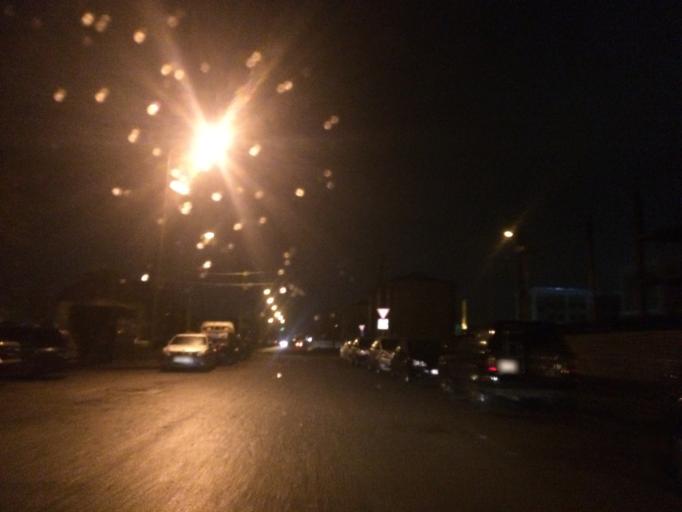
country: KZ
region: Astana Qalasy
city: Astana
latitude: 51.1974
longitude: 71.3865
